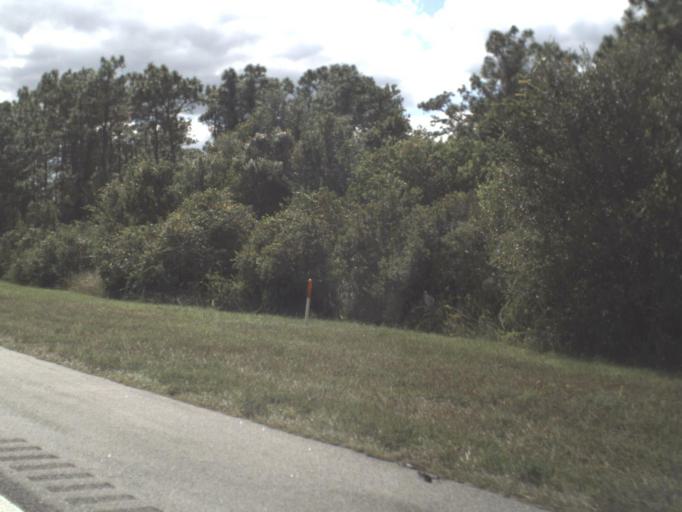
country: US
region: Florida
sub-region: Osceola County
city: Saint Cloud
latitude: 28.2041
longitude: -81.3069
